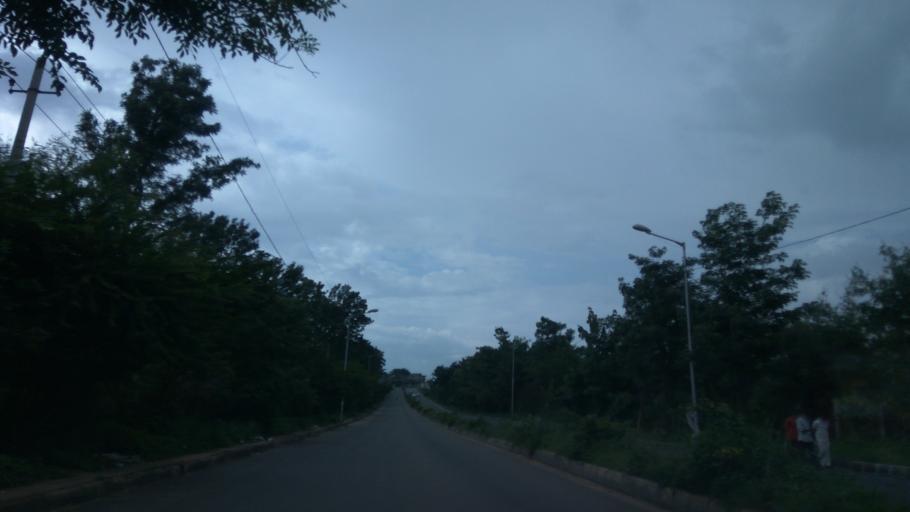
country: IN
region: Karnataka
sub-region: Bangalore Urban
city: Yelahanka
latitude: 13.1041
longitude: 77.6344
